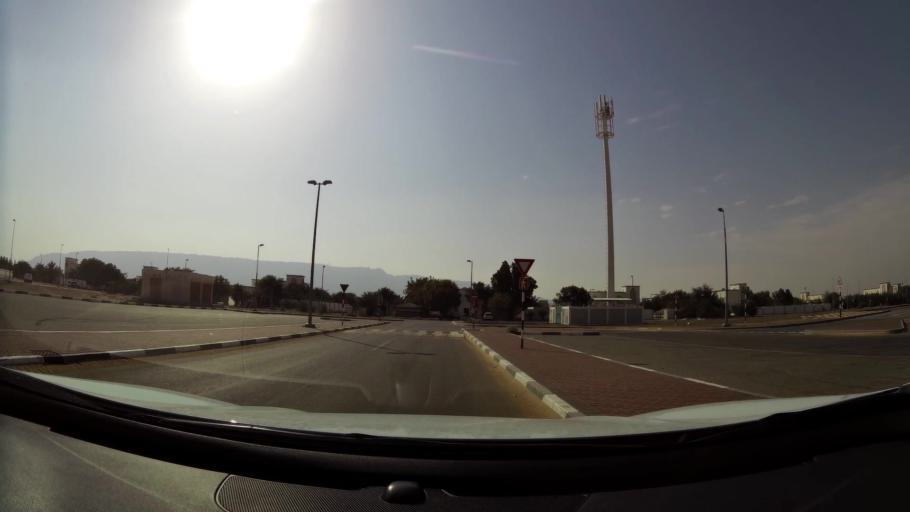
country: AE
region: Abu Dhabi
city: Al Ain
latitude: 24.0715
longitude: 55.8662
